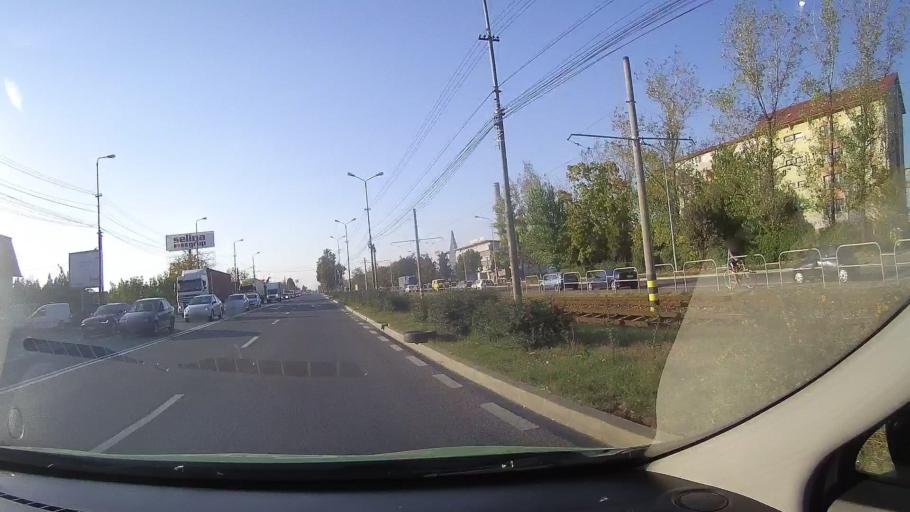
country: RO
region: Bihor
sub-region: Comuna Biharea
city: Oradea
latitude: 47.0775
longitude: 21.9003
